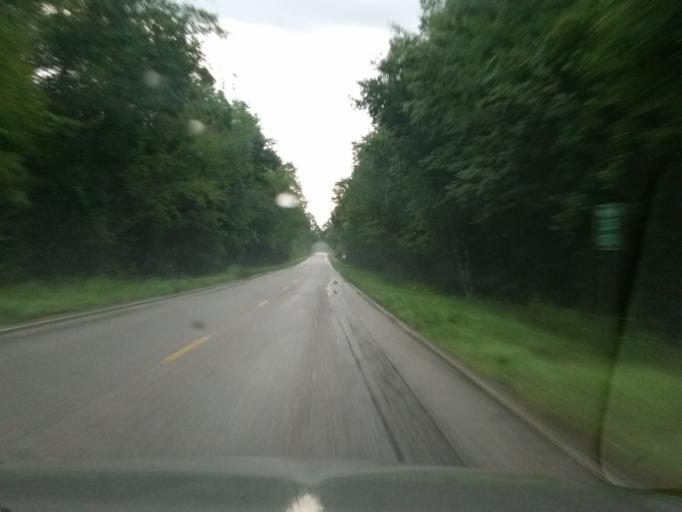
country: US
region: Florida
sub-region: Escambia County
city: Cantonment
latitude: 30.6069
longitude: -87.4081
